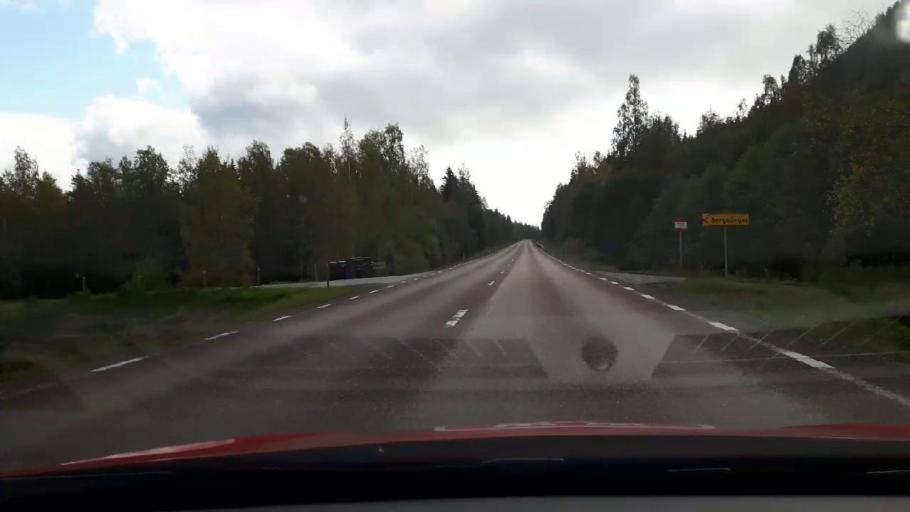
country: SE
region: Gaevleborg
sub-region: Bollnas Kommun
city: Arbra
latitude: 61.5617
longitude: 16.3380
